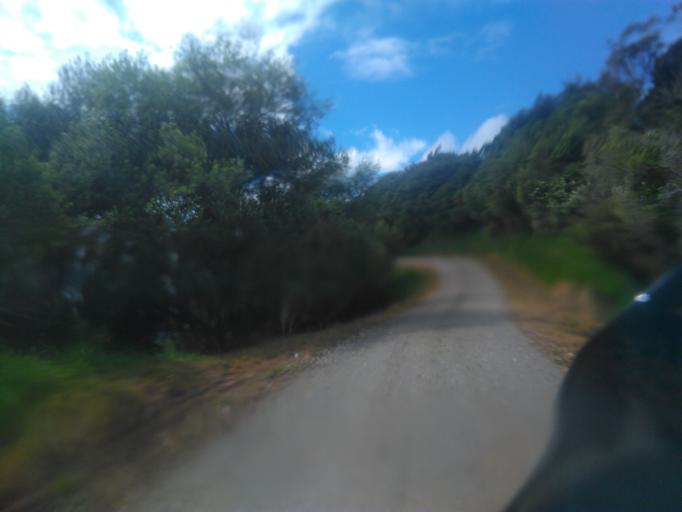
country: NZ
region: Hawke's Bay
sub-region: Wairoa District
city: Wairoa
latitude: -38.7712
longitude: 177.6387
